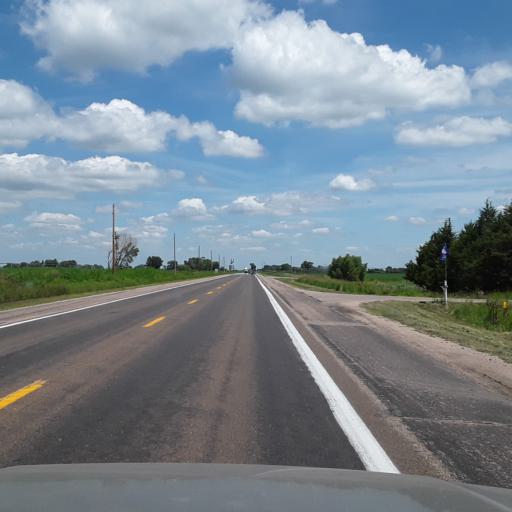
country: US
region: Nebraska
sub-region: Merrick County
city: Central City
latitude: 41.1556
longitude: -97.9364
